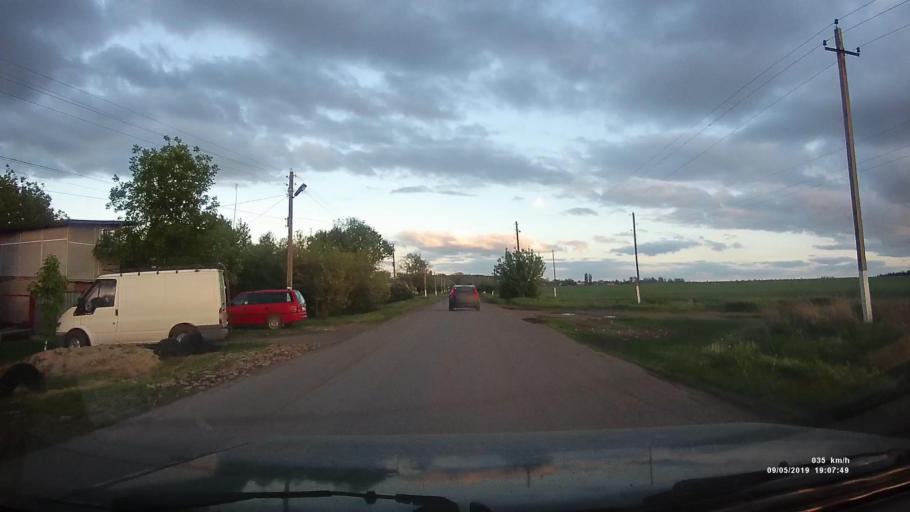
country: RU
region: Krasnodarskiy
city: Kanelovskaya
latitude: 46.7328
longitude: 39.1991
